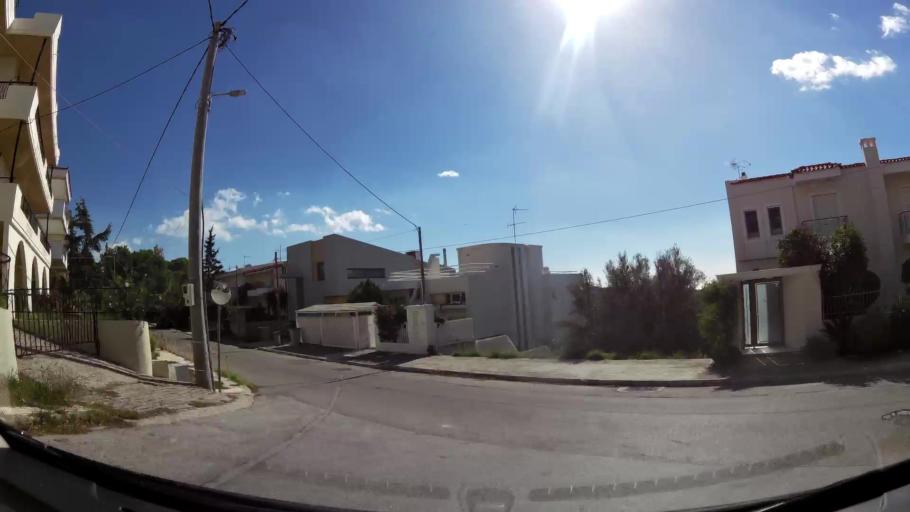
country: GR
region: Attica
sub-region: Nomarchia Anatolikis Attikis
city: Voula
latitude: 37.8484
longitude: 23.7817
